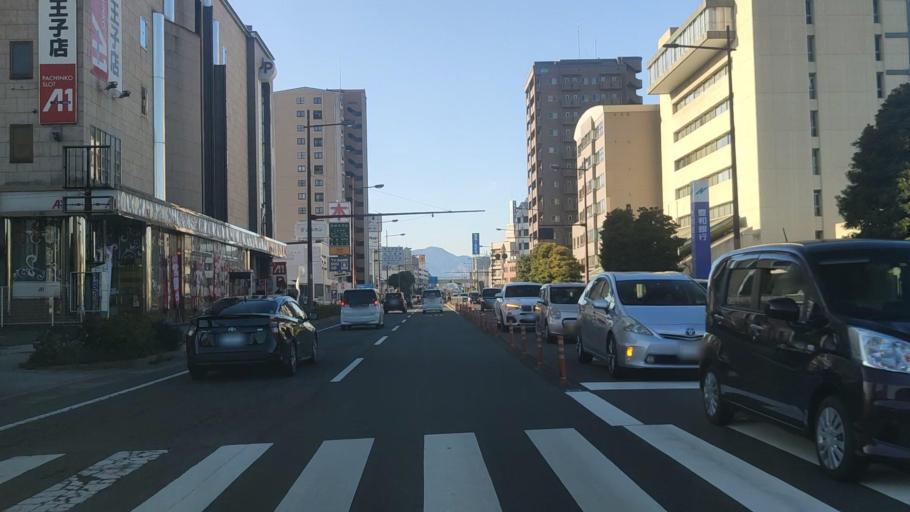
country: JP
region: Oita
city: Oita
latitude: 33.2407
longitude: 131.5942
